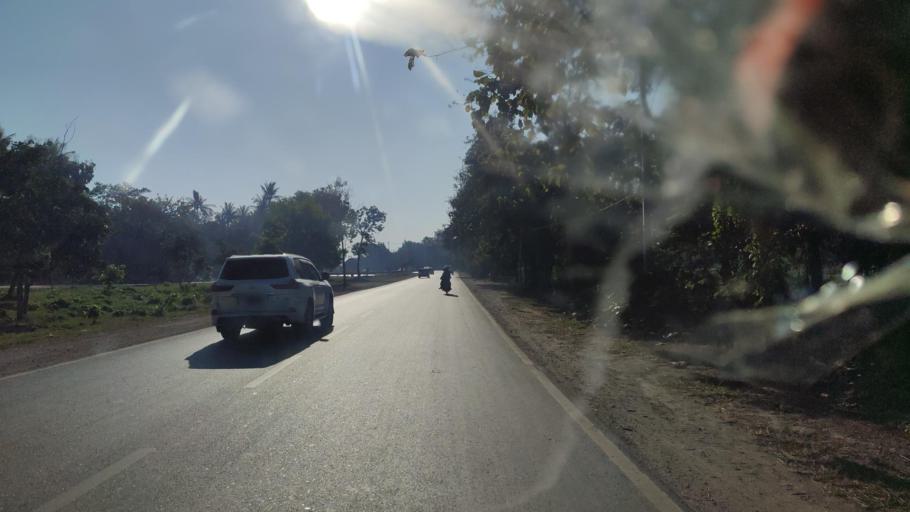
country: MM
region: Mandalay
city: Mandalay
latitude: 21.9123
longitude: 96.1717
